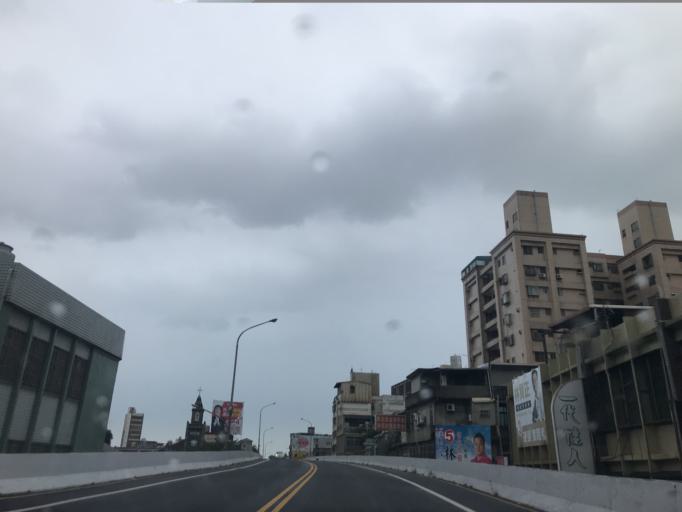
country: TW
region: Taiwan
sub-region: Hsinchu
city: Zhubei
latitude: 24.8366
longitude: 121.0095
